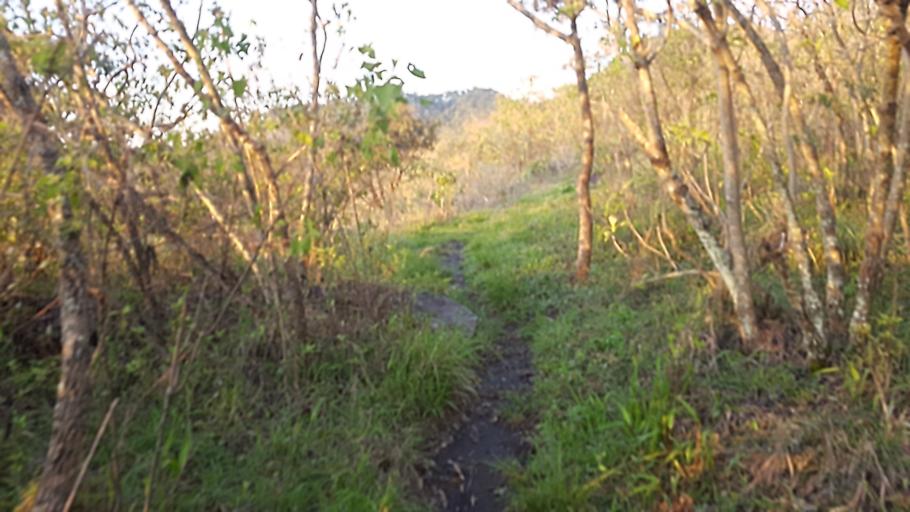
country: MX
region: Nayarit
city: Tepic
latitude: 21.5013
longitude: -104.9284
